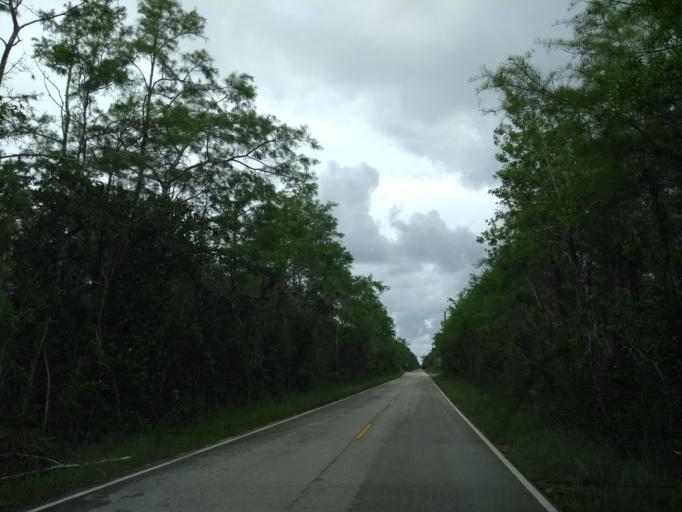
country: US
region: Florida
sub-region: Miami-Dade County
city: The Hammocks
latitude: 25.7613
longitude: -80.8980
